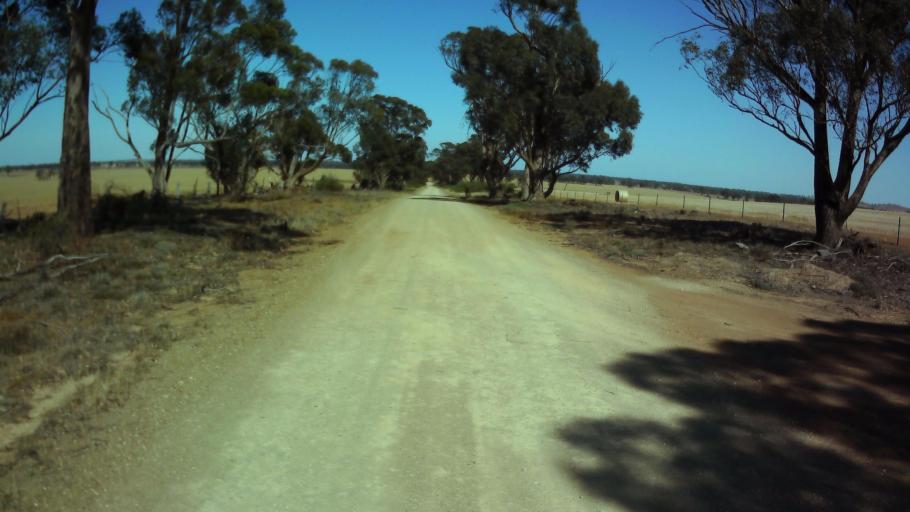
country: AU
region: New South Wales
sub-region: Weddin
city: Grenfell
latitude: -33.8801
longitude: 147.8823
